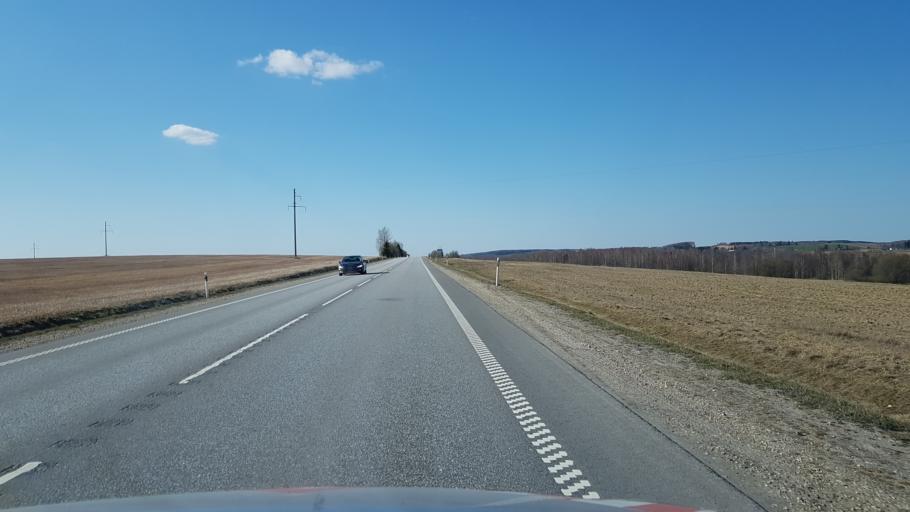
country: EE
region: Tartu
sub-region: Tartu linn
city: Tartu
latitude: 58.4511
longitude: 26.8032
